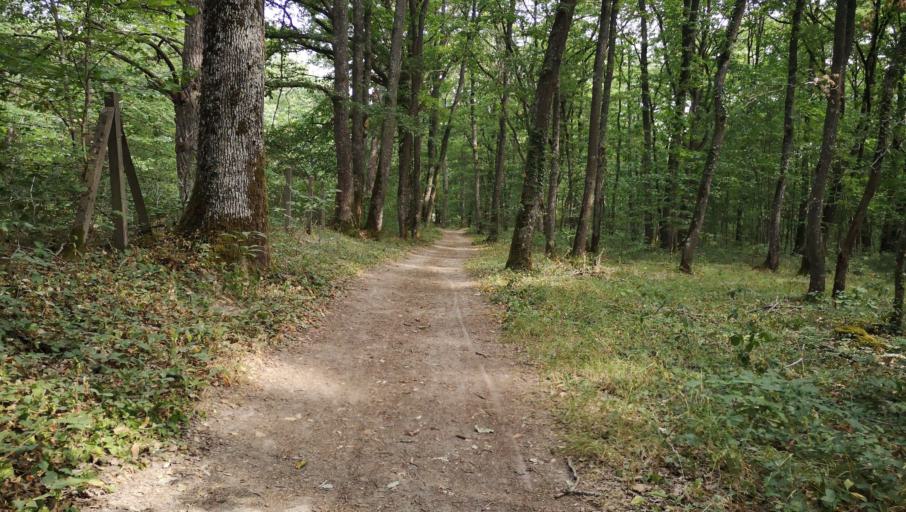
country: FR
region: Centre
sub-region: Departement du Loiret
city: Chanteau
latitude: 47.9425
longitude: 1.9821
